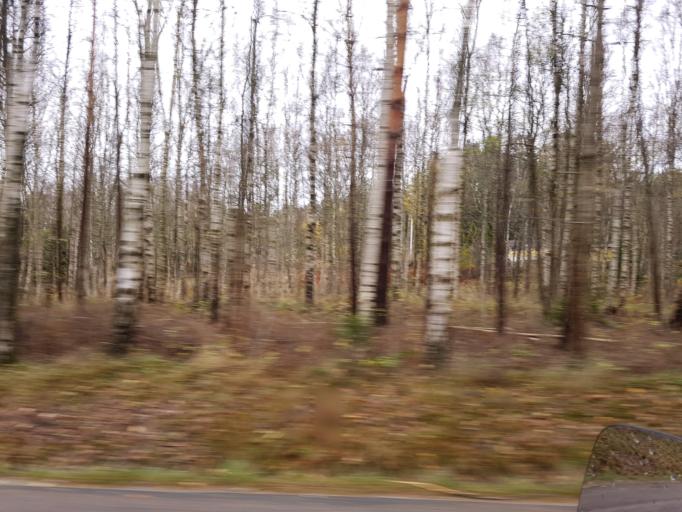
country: SE
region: Vaestra Goetaland
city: Svanesund
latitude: 58.1630
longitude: 11.8173
